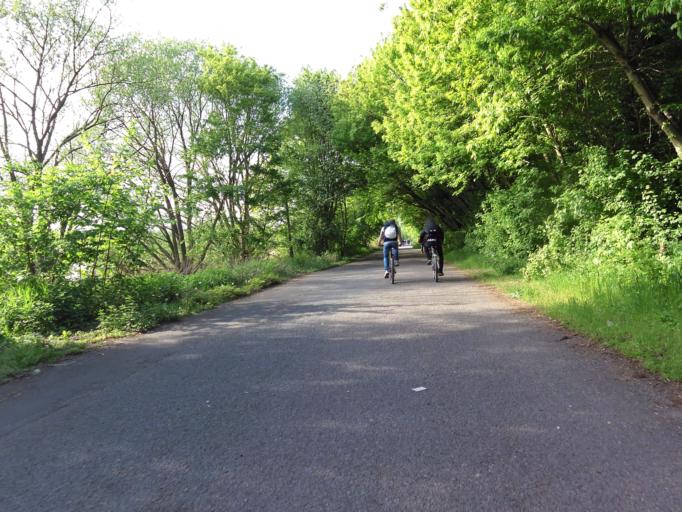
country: DE
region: Saxony
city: Leipzig
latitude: 51.3427
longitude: 12.3468
